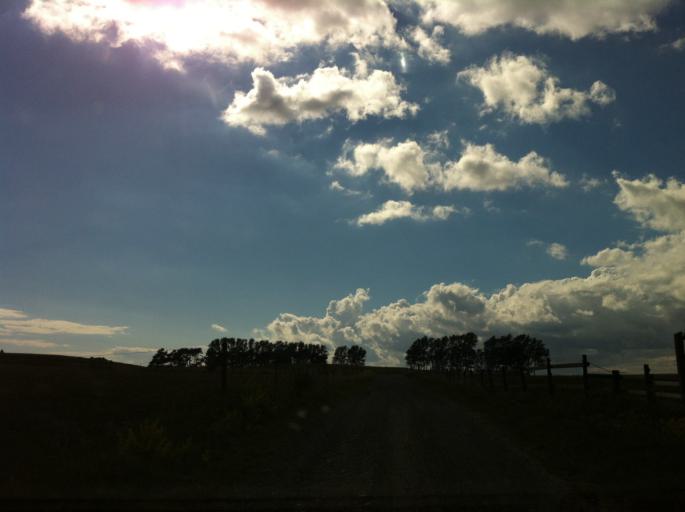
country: SE
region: Skane
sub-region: Ystads Kommun
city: Kopingebro
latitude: 55.3916
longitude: 14.0485
